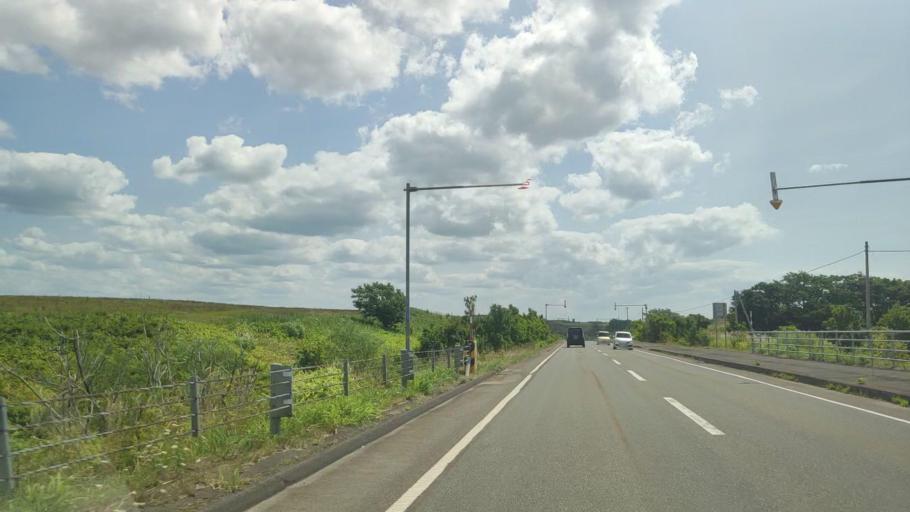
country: JP
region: Hokkaido
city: Makubetsu
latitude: 44.7989
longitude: 141.7879
